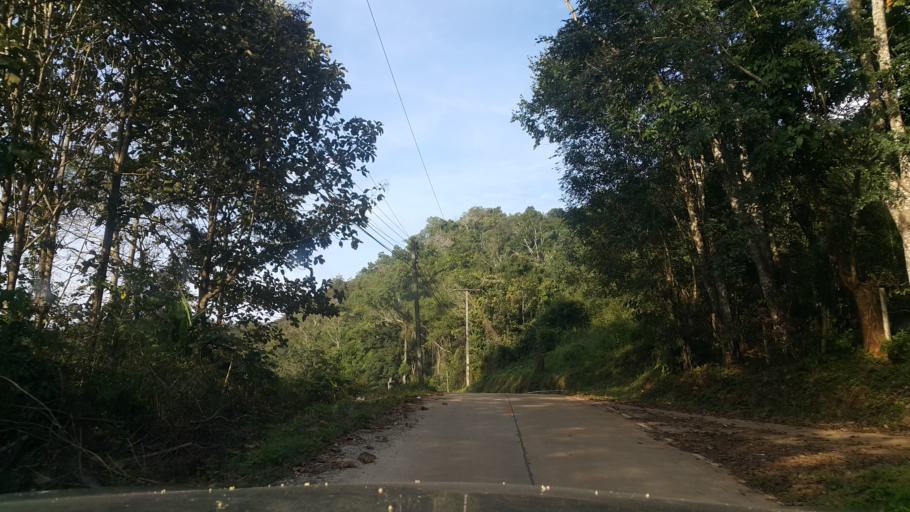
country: TH
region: Chiang Mai
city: Samoeng
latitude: 19.0143
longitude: 98.6734
